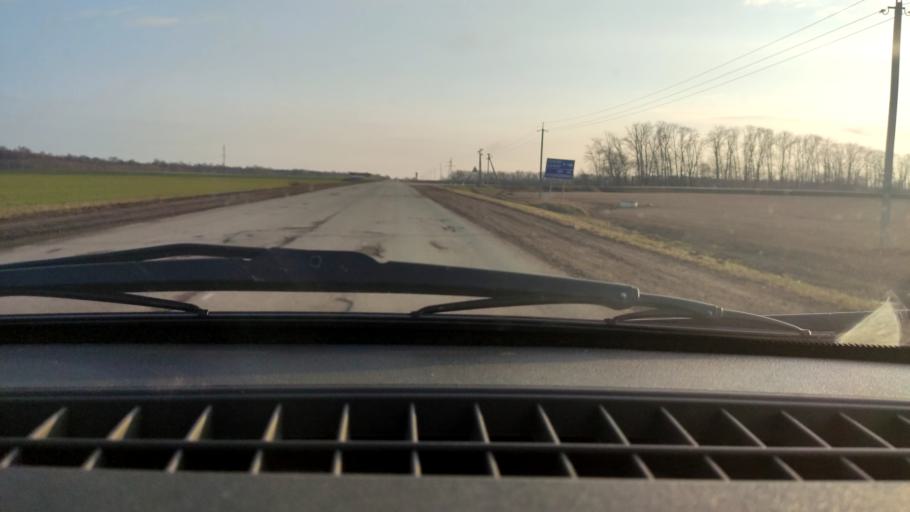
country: RU
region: Bashkortostan
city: Chishmy
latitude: 54.5641
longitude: 55.3473
